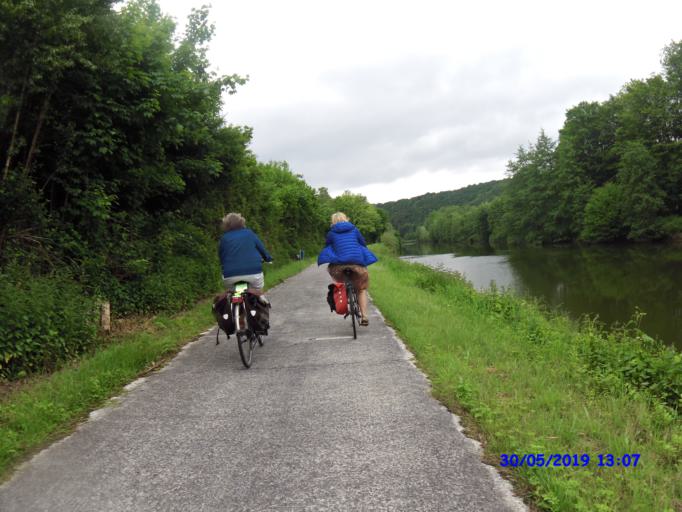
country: BE
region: Wallonia
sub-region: Province du Hainaut
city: Thuin
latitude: 50.3552
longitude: 4.3097
